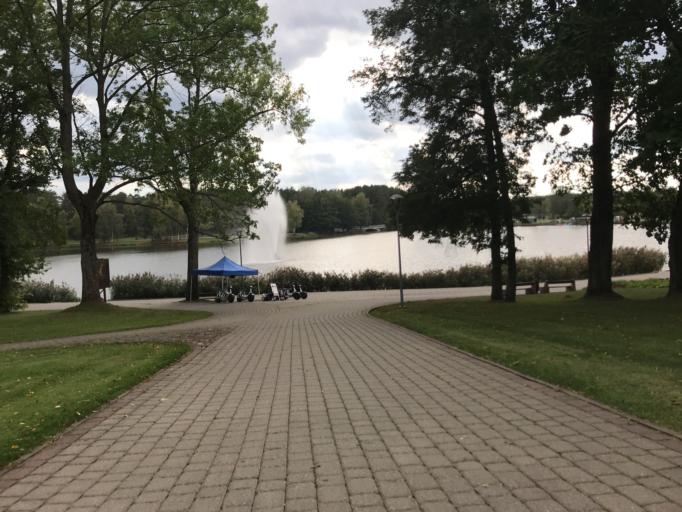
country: LT
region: Alytaus apskritis
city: Druskininkai
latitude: 54.0160
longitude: 23.9752
